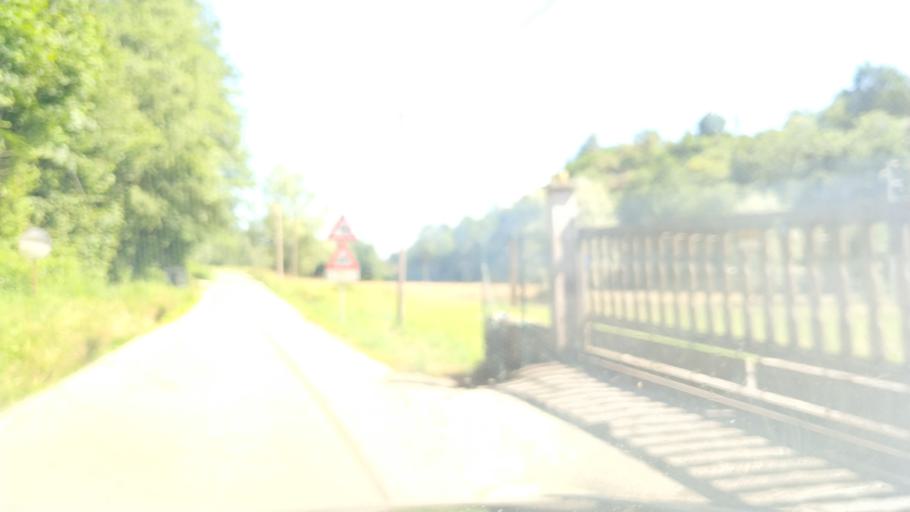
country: IT
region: Piedmont
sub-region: Provincia di Torino
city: Baldissero Canavese
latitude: 45.4089
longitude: 7.7208
